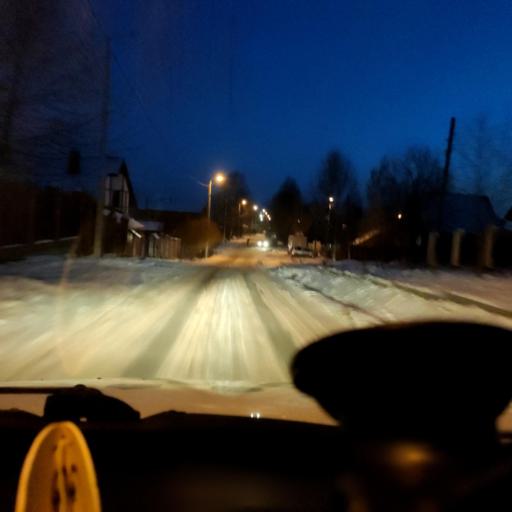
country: RU
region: Perm
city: Froly
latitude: 57.9491
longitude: 56.3023
